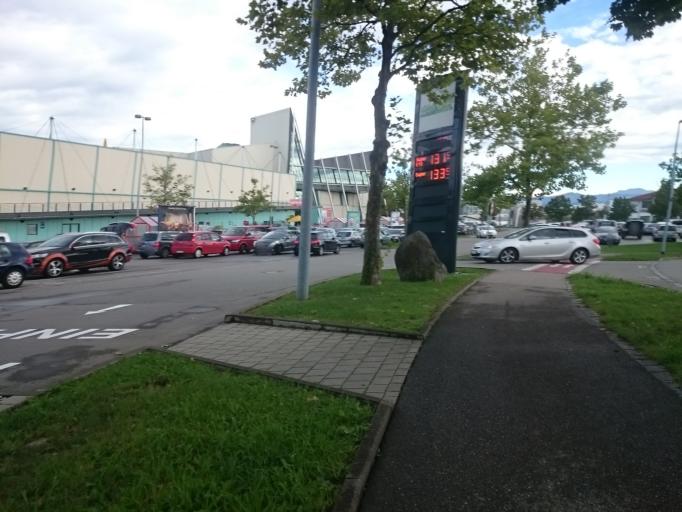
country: DE
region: Bavaria
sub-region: Swabia
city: Kempten (Allgaeu)
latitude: 47.7488
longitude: 10.3201
